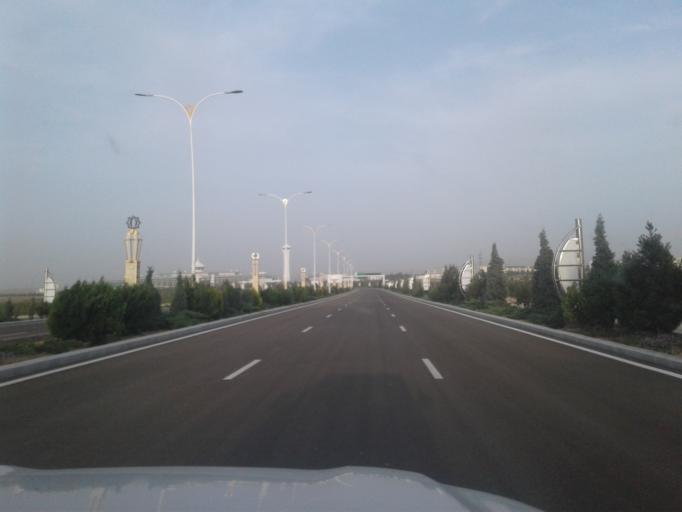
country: TM
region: Balkan
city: Turkmenbasy
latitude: 40.0444
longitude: 52.9826
